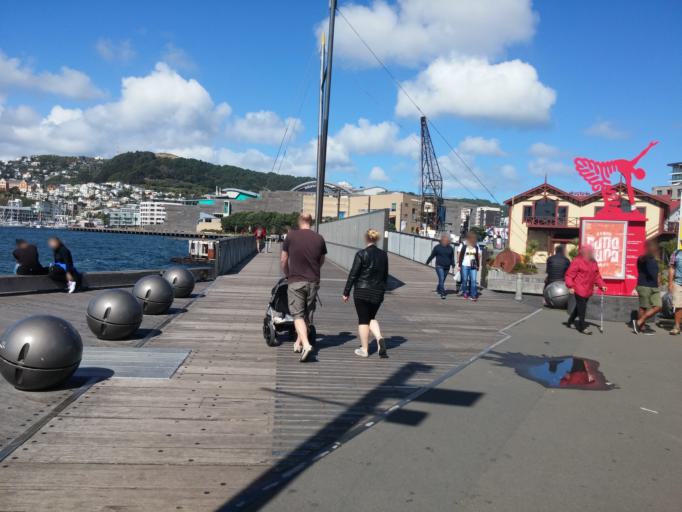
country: NZ
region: Wellington
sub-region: Wellington City
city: Wellington
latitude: -41.2879
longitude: 174.7794
